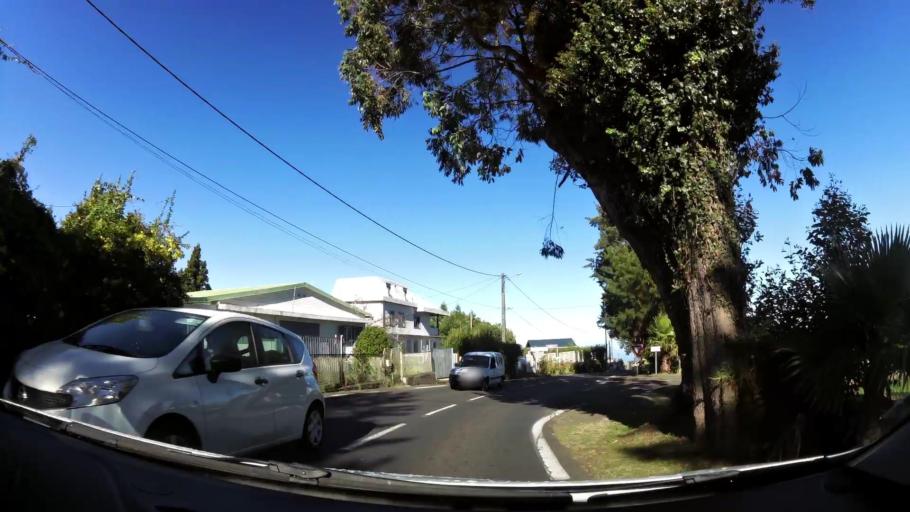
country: RE
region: Reunion
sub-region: Reunion
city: Le Tampon
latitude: -21.2211
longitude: 55.5598
